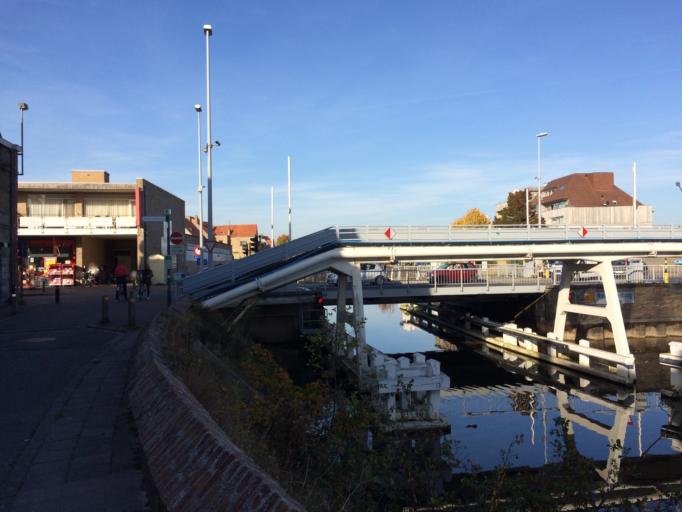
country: BE
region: Flanders
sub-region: Provincie West-Vlaanderen
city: Veurne
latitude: 51.0727
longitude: 2.6675
